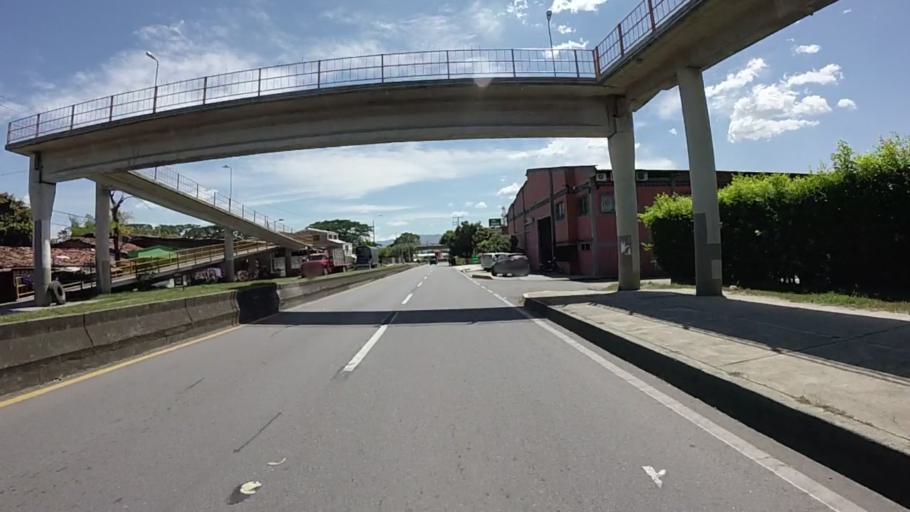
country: CO
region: Valle del Cauca
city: Cartago
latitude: 4.7322
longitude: -75.9072
